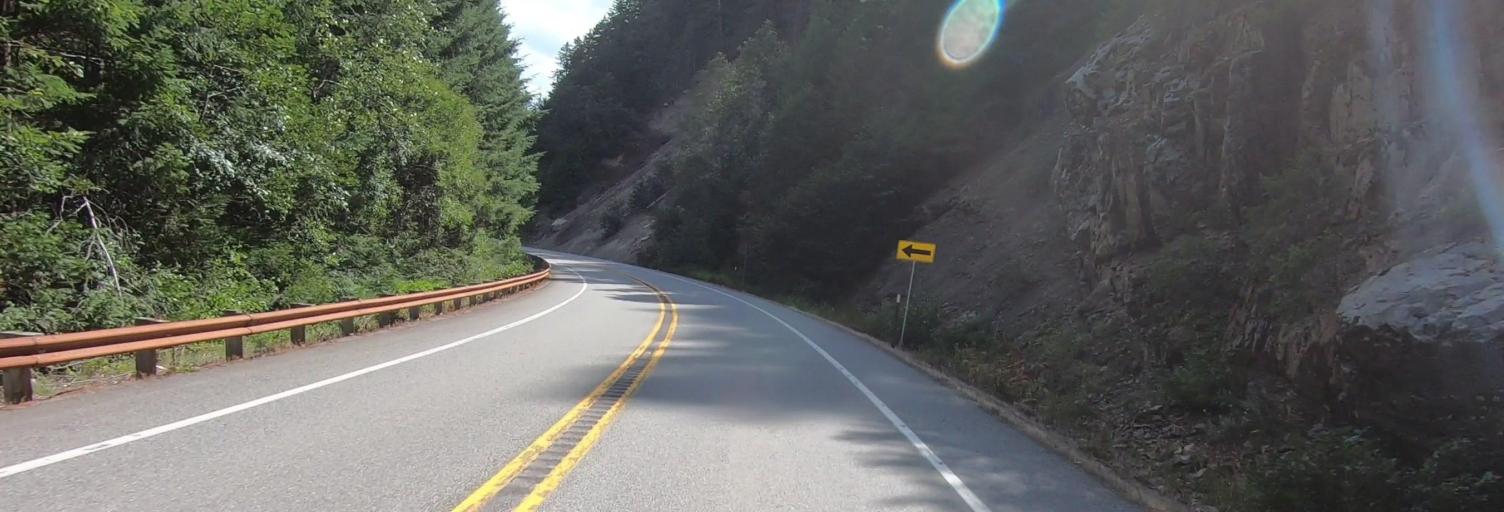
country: US
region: Washington
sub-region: Snohomish County
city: Darrington
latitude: 48.6866
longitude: -120.9085
